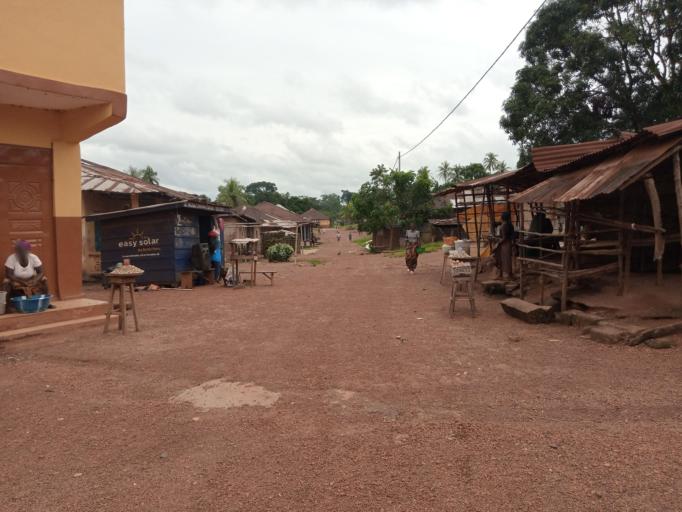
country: SL
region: Southern Province
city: Largo
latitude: 8.2040
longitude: -12.0598
